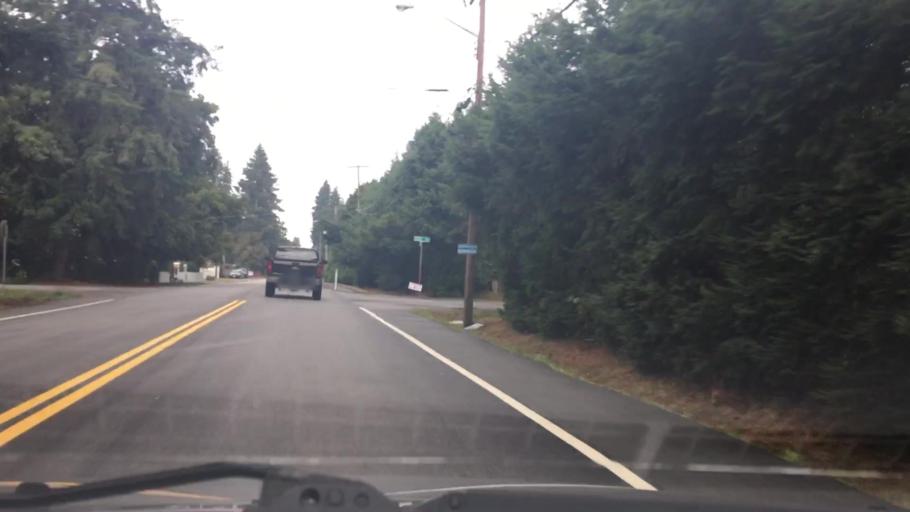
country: CA
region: British Columbia
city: Langley
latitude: 49.1040
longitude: -122.5312
